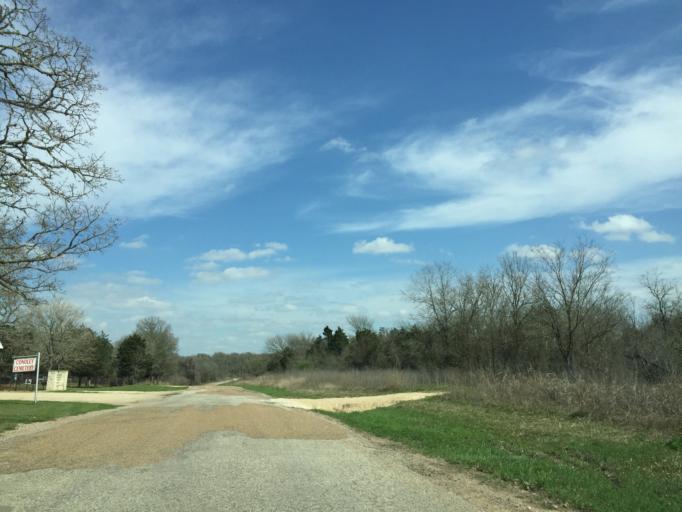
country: US
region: Texas
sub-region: Milam County
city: Thorndale
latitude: 30.5577
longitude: -97.1765
